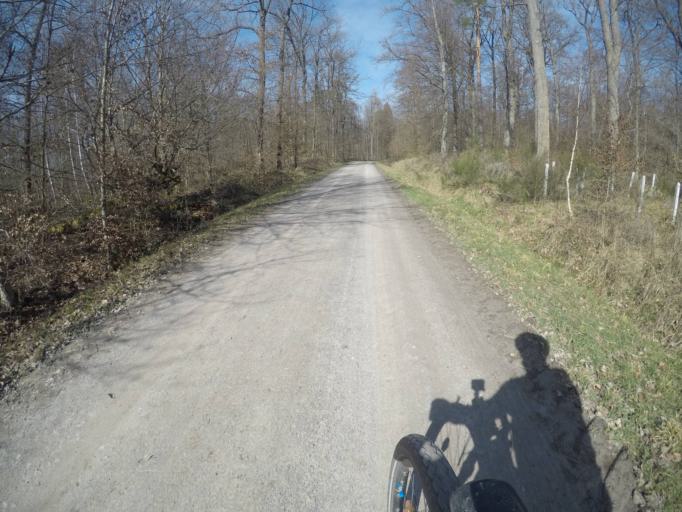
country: DE
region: Baden-Wuerttemberg
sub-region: Regierungsbezirk Stuttgart
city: Gerlingen
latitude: 48.7715
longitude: 9.0740
